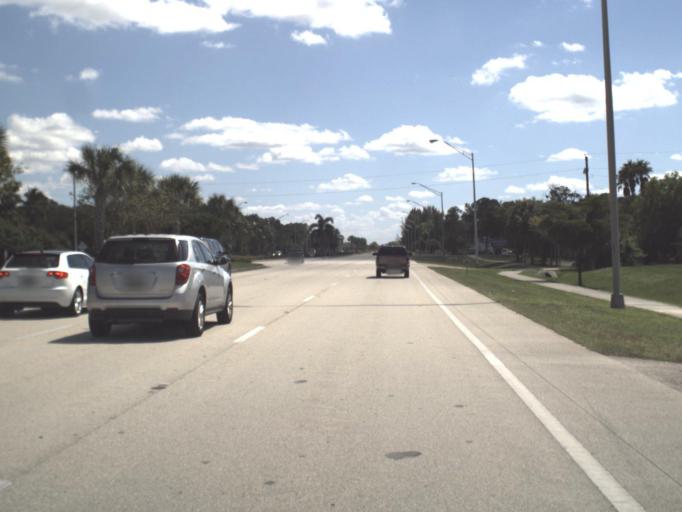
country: US
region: Florida
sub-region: Collier County
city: Naples Manor
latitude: 26.0900
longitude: -81.7325
